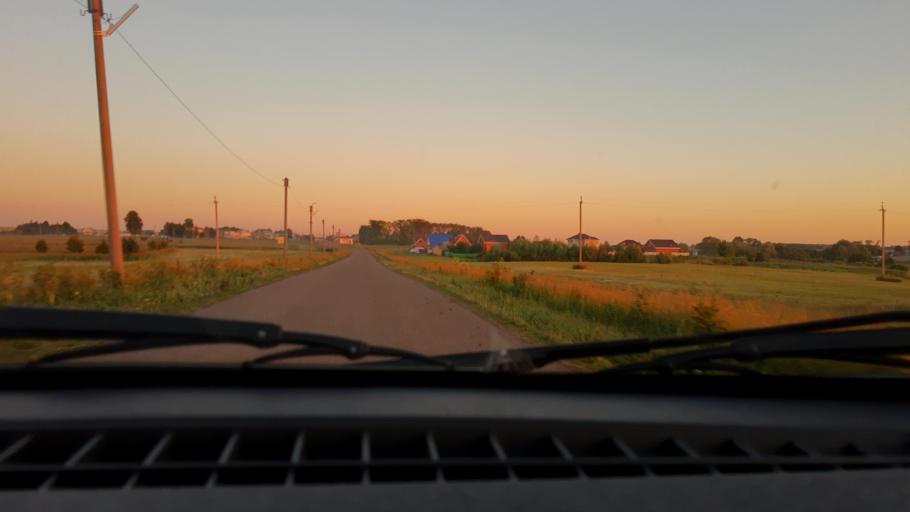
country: RU
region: Bashkortostan
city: Asanovo
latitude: 54.8957
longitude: 55.6258
